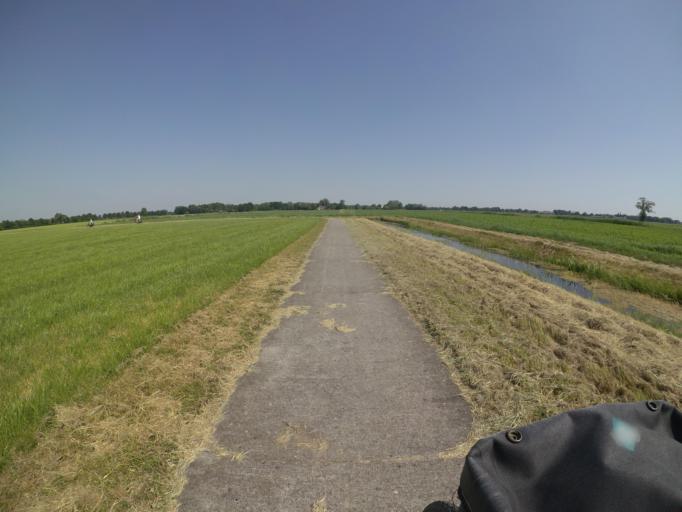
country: NL
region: Drenthe
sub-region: Gemeente De Wolden
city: Ruinen
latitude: 52.6813
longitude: 6.3180
